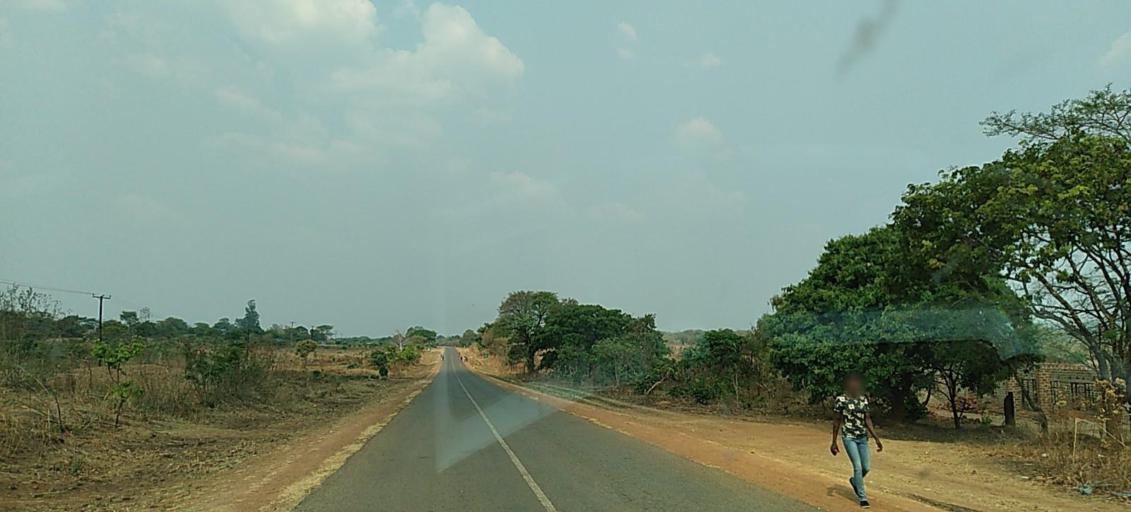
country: ZM
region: North-Western
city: Kabompo
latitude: -13.5910
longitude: 24.2152
